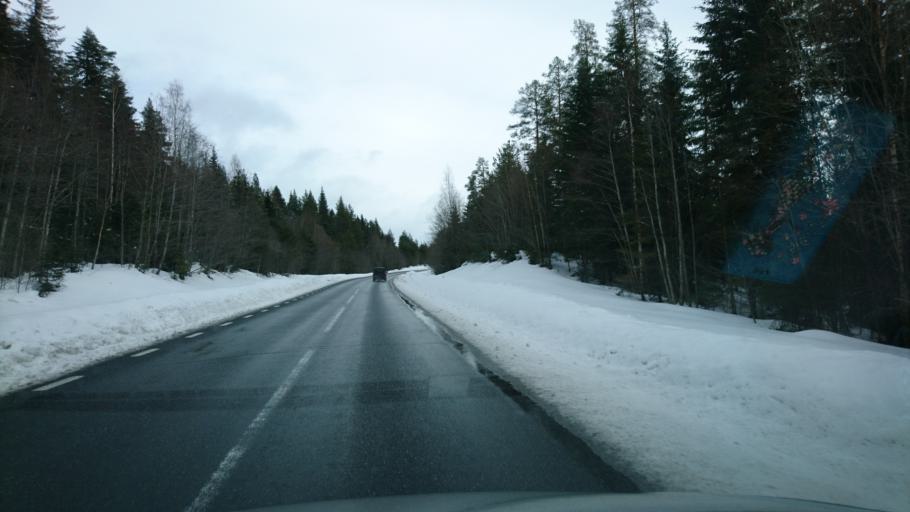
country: SE
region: Vaesternorrland
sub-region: Solleftea Kommun
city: Solleftea
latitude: 63.0556
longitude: 17.0395
